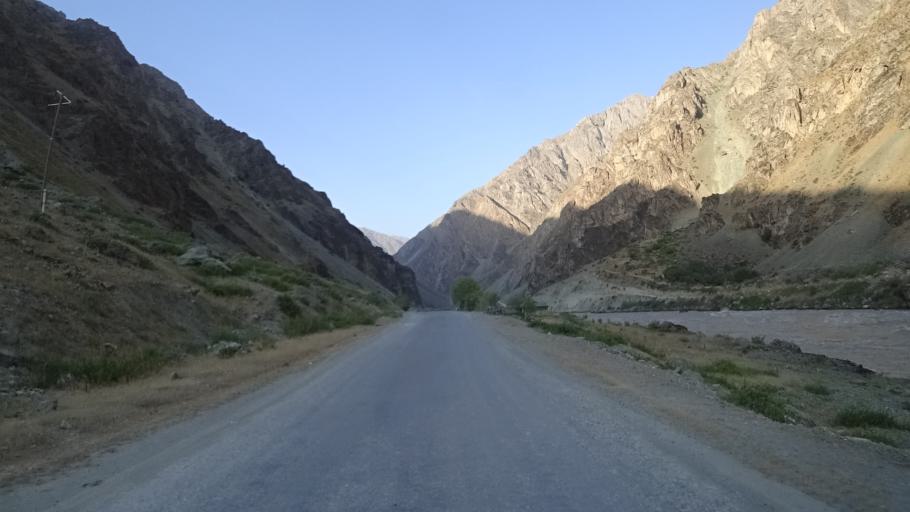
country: TJ
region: Gorno-Badakhshan
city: Qalaikhumb
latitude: 38.4189
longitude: 70.7383
